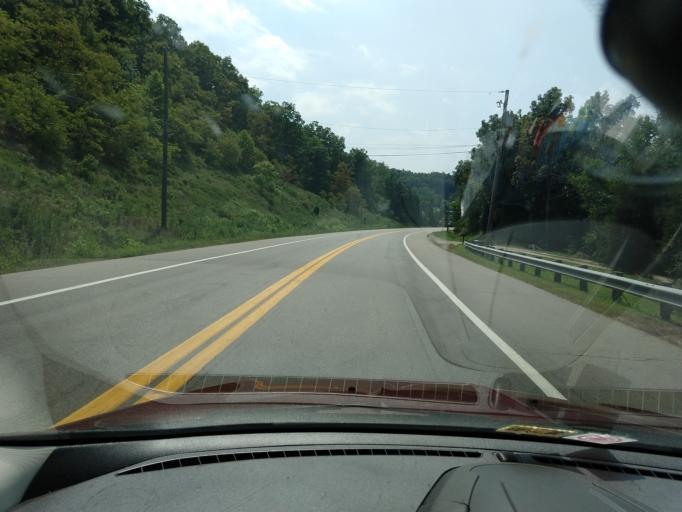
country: US
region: West Virginia
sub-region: Jackson County
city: Ravenswood
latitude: 38.8594
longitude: -81.8051
